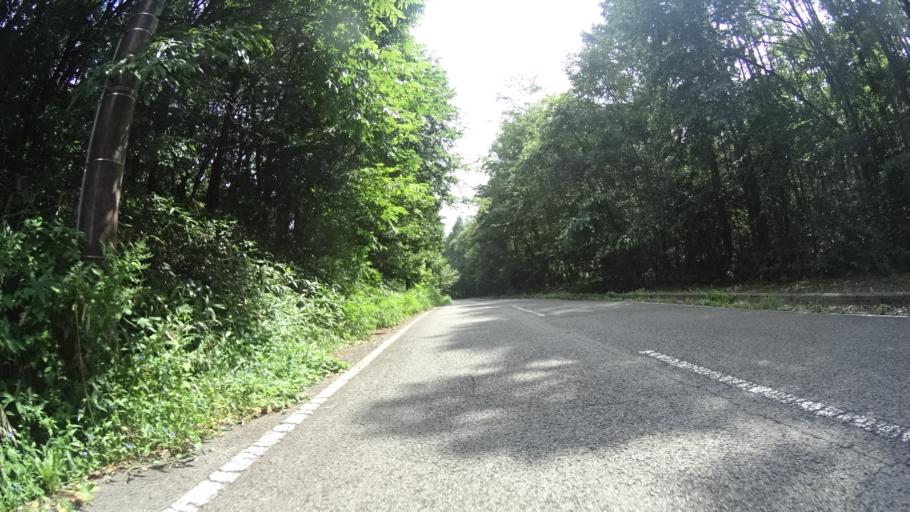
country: JP
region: Yamanashi
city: Nirasaki
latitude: 35.9087
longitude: 138.4265
